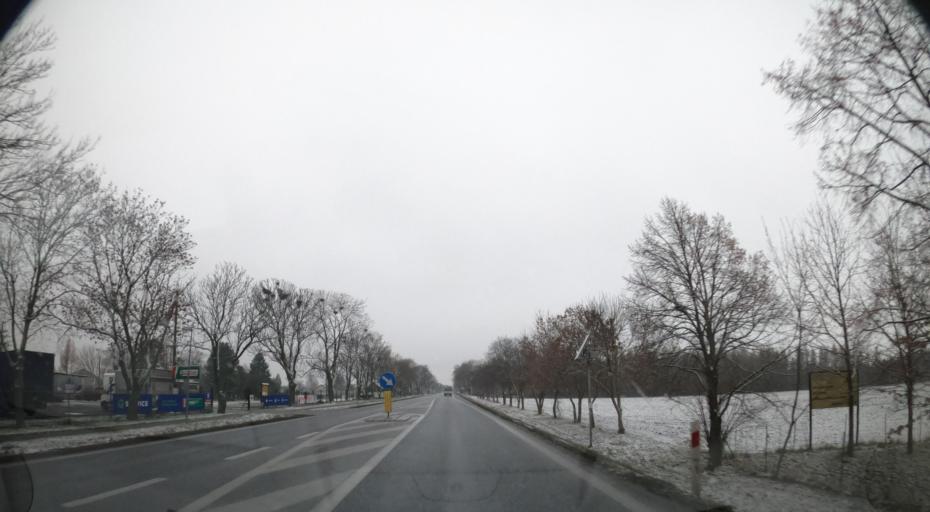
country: PL
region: Masovian Voivodeship
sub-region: Powiat warszawski zachodni
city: Bieniewice
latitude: 52.2013
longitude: 20.5507
